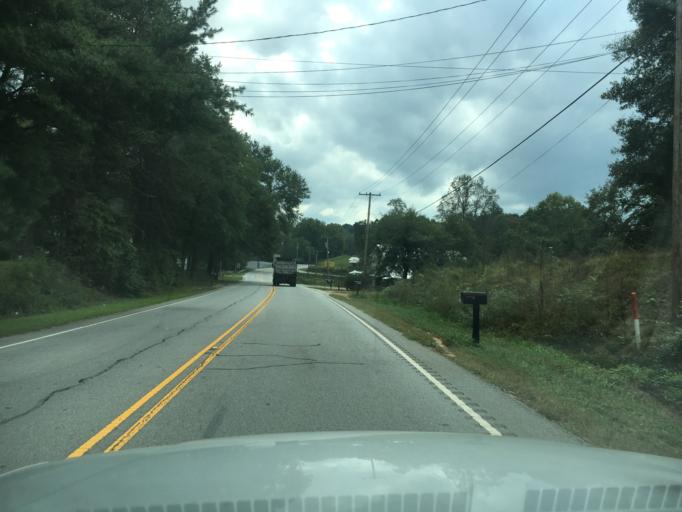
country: US
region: South Carolina
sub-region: Greenville County
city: Greer
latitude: 34.9819
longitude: -82.2452
